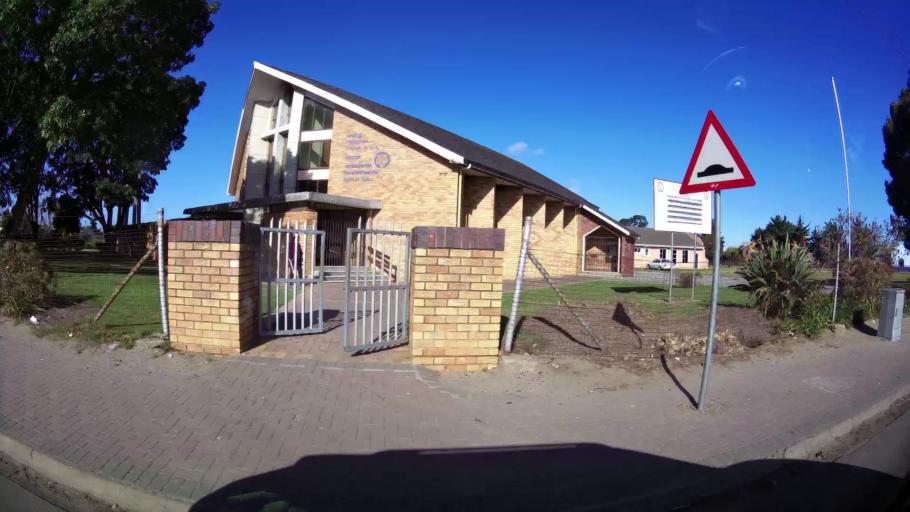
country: ZA
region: Western Cape
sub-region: Eden District Municipality
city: George
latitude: -33.9726
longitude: 22.4787
